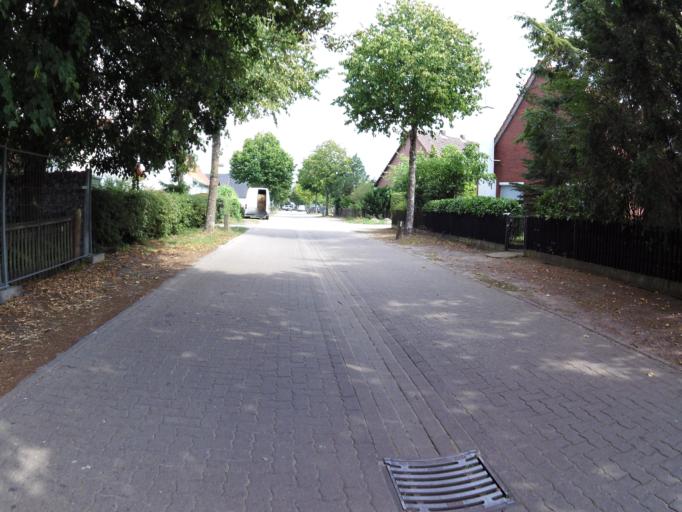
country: DE
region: Lower Saxony
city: Nienburg
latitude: 52.6122
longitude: 9.2049
